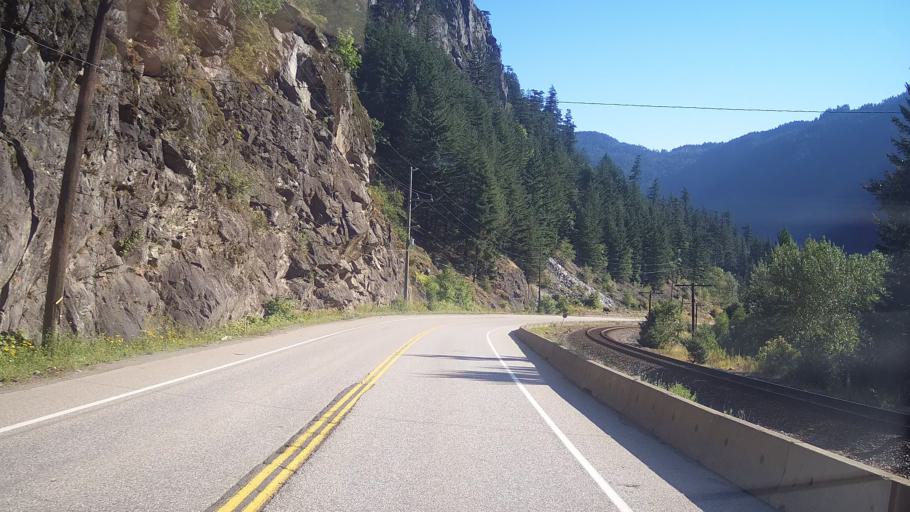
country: CA
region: British Columbia
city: Hope
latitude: 49.6180
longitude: -121.4057
